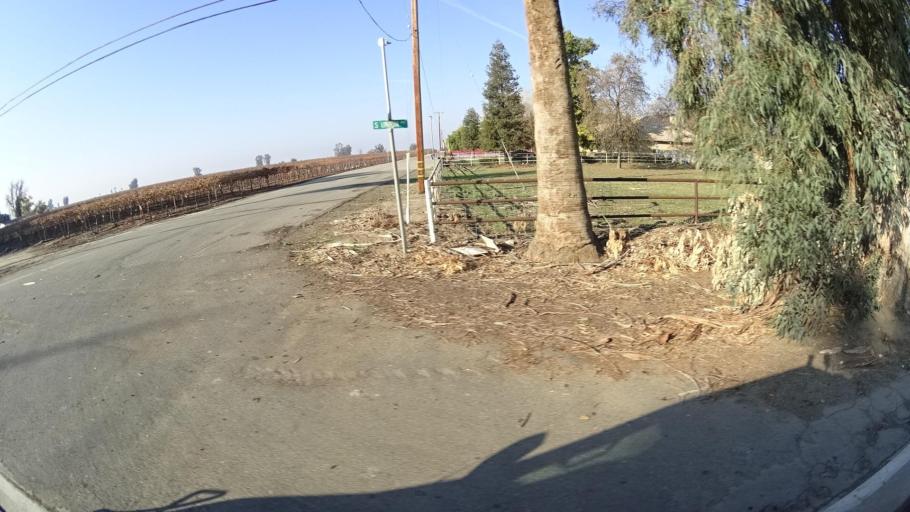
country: US
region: California
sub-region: Kern County
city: Greenfield
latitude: 35.2180
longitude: -119.0033
